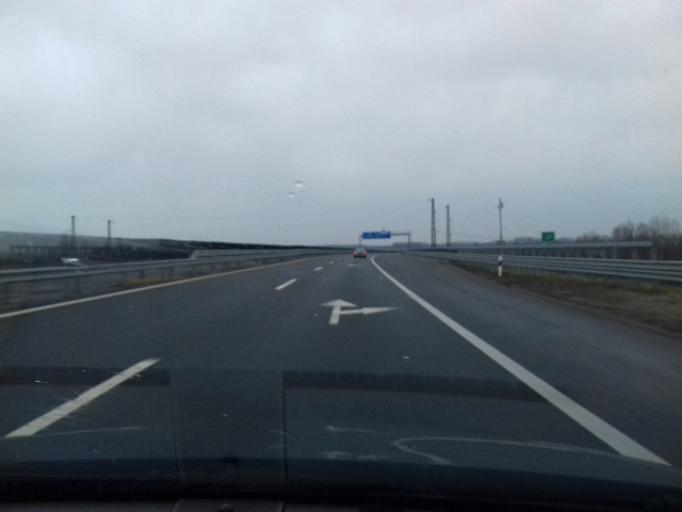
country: HU
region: Szabolcs-Szatmar-Bereg
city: Nyiregyhaza
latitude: 47.8832
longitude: 21.7156
